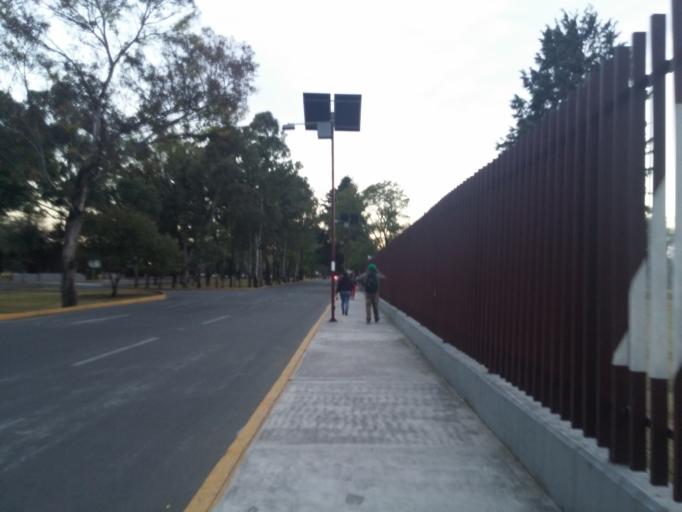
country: MX
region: Mexico
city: Colonia Lindavista
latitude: 19.5018
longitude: -99.1398
